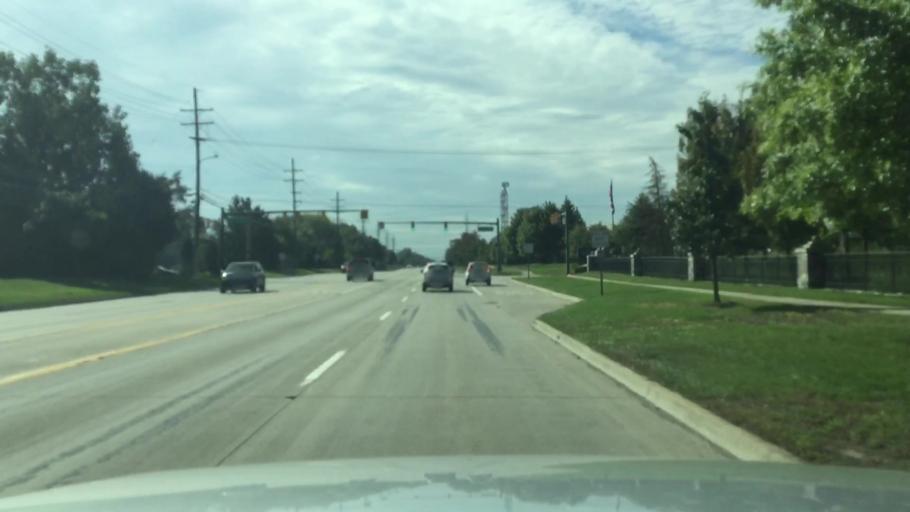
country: US
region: Michigan
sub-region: Wayne County
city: Canton
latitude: 42.3156
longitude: -83.4877
